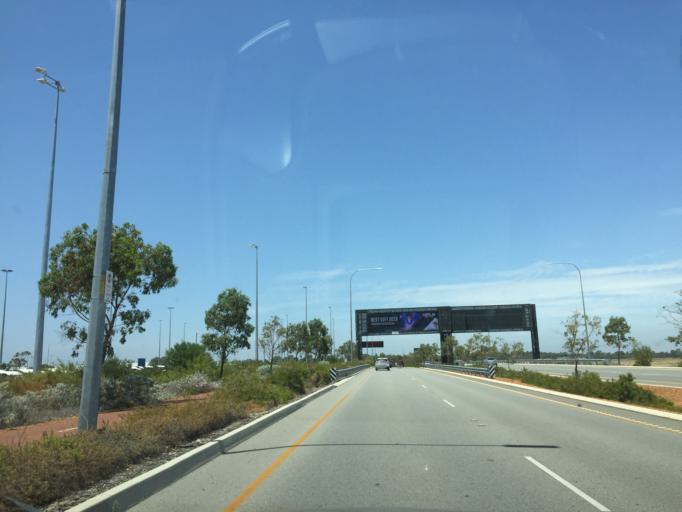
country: AU
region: Western Australia
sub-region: Belmont
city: Redcliffe
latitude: -31.9514
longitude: 115.9702
